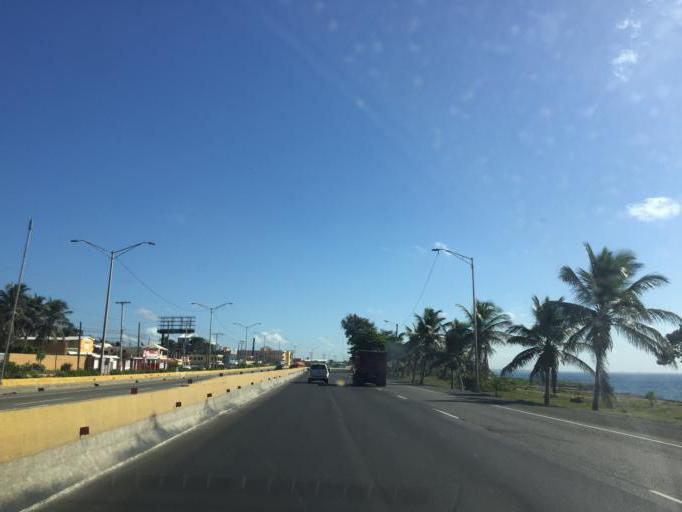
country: DO
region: Santo Domingo
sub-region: Santo Domingo
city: Santo Domingo Este
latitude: 18.4656
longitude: -69.7974
